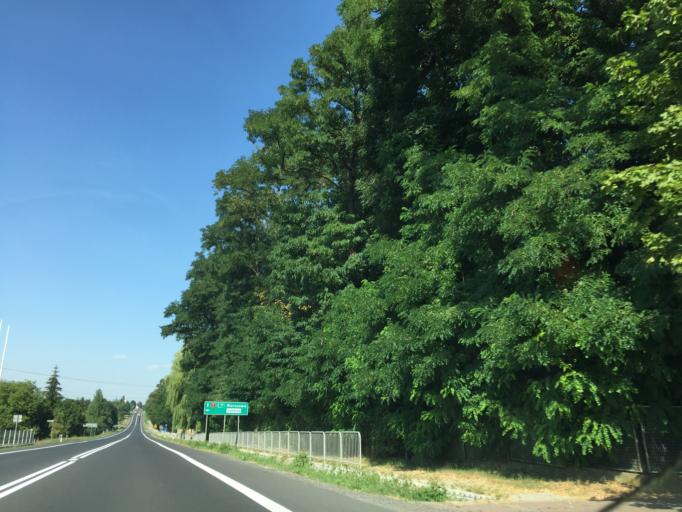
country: PL
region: Lesser Poland Voivodeship
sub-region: Powiat krakowski
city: Michalowice
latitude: 50.1923
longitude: 20.0046
